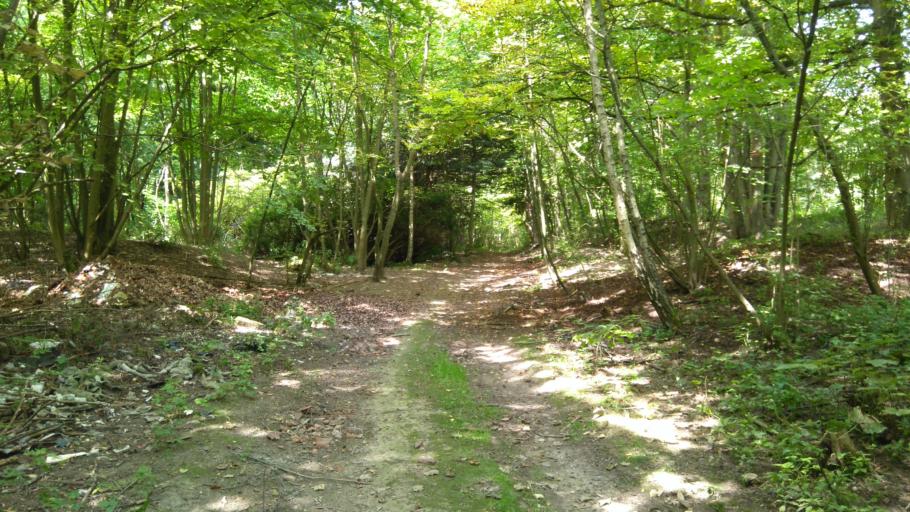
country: FR
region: Picardie
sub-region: Departement de l'Oise
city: Saint-Maximin
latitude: 49.2397
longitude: 2.4538
